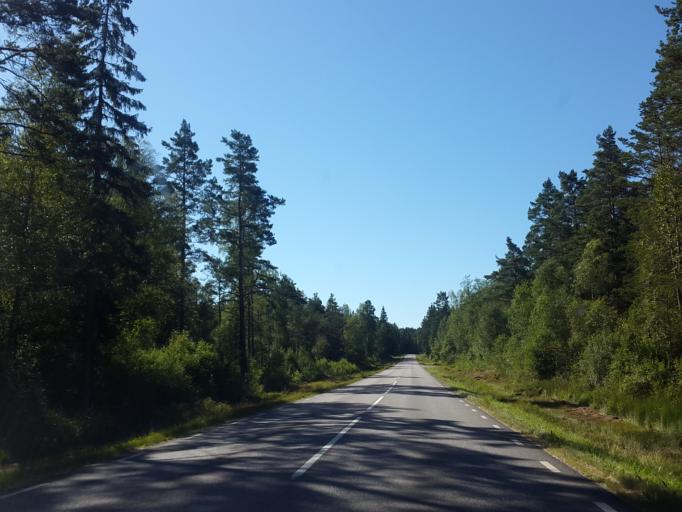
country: SE
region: Vaestra Goetaland
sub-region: Herrljunga Kommun
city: Herrljunga
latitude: 58.0330
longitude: 13.0473
